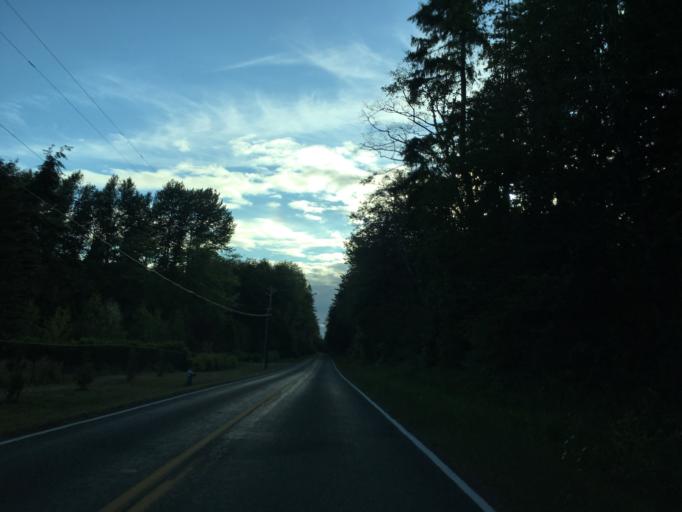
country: US
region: Washington
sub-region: Whatcom County
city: Birch Bay
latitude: 48.9406
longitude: -122.8108
